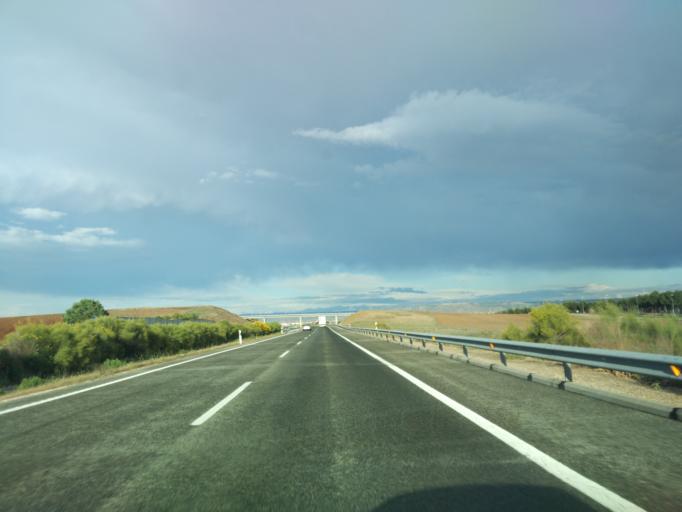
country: ES
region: Madrid
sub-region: Provincia de Madrid
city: Ajalvir
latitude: 40.5059
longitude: -3.4552
